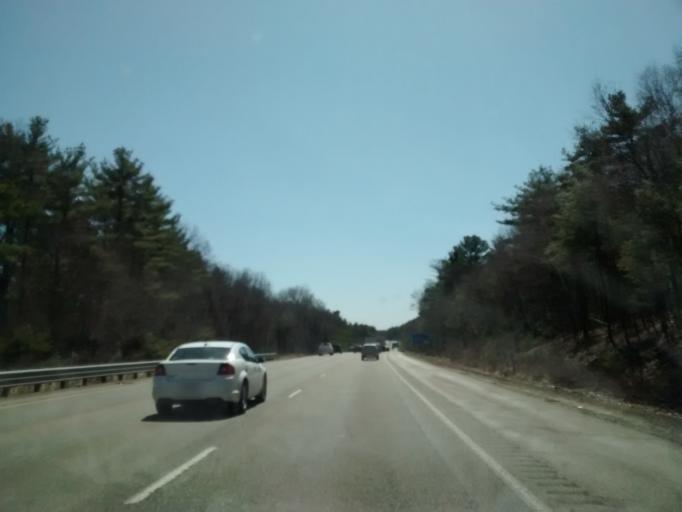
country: US
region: Massachusetts
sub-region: Middlesex County
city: Hopkinton
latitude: 42.2325
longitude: -71.5514
